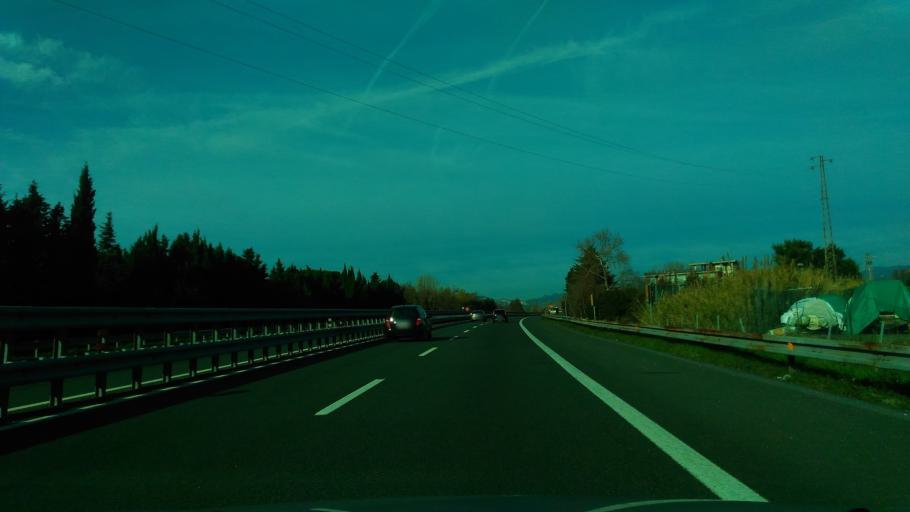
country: IT
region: Liguria
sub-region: Provincia di La Spezia
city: Ameglia
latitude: 44.0758
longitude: 9.9834
